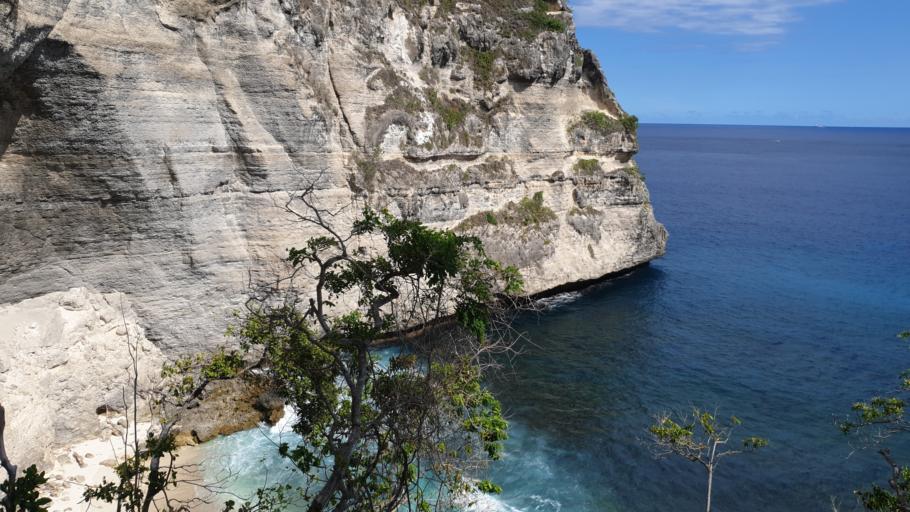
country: ID
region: Bali
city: Tanglad
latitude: -8.7746
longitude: 115.6201
